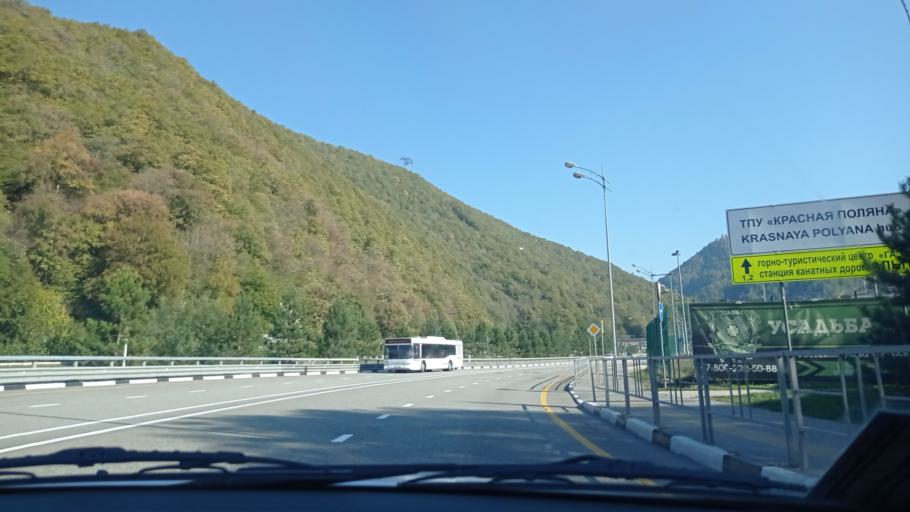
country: RU
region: Krasnodarskiy
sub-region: Sochi City
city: Krasnaya Polyana
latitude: 43.6792
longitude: 40.2768
